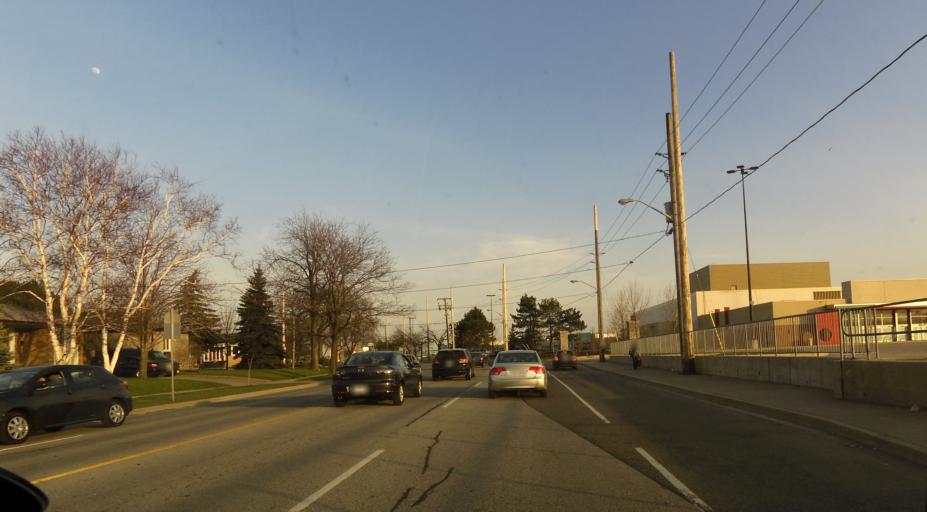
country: CA
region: Ontario
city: Etobicoke
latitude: 43.6340
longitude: -79.5565
